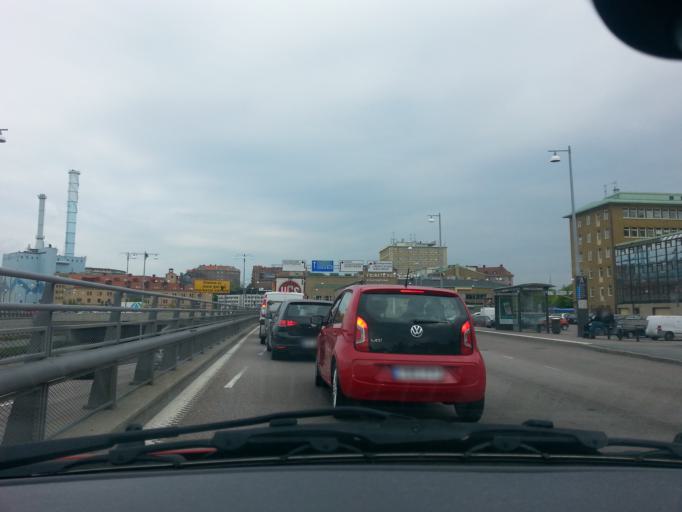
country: SE
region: Vaestra Goetaland
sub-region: Goteborg
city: Goeteborg
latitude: 57.7010
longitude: 11.9489
